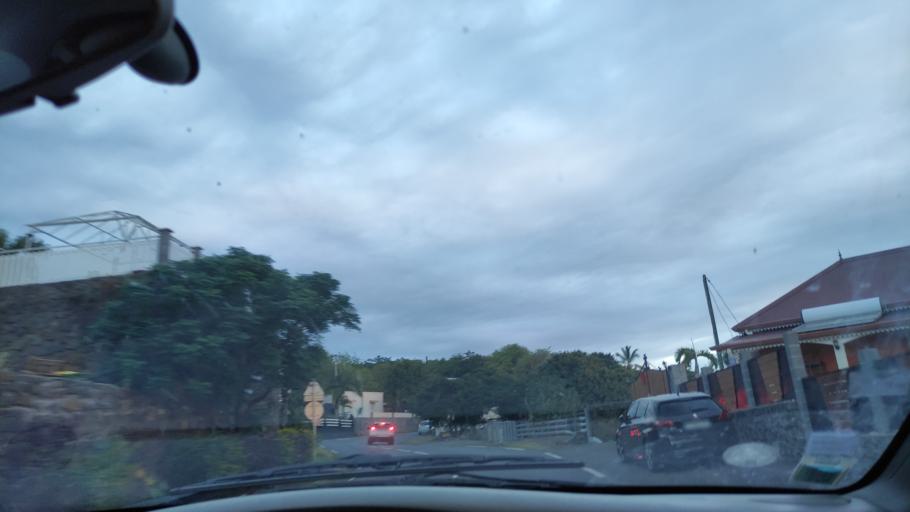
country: RE
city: Piton Saint-Leu
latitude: -21.2104
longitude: 55.3001
